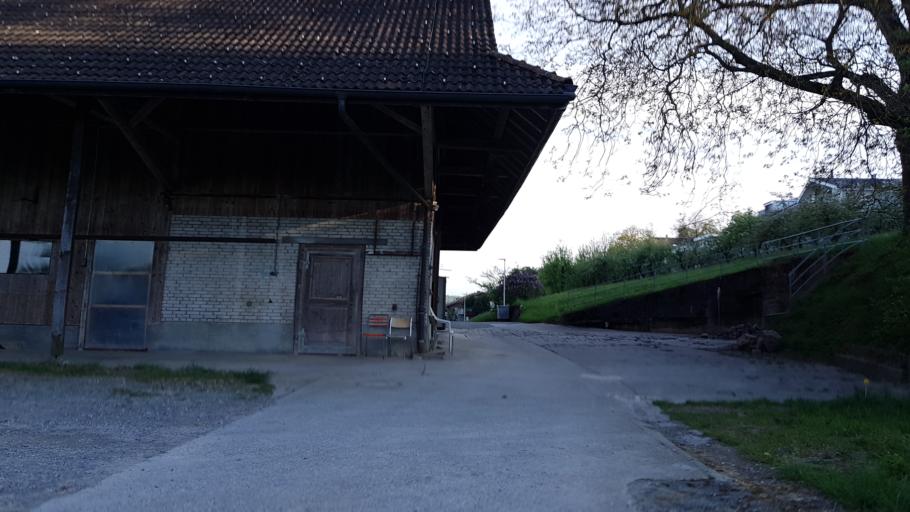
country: CH
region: Aargau
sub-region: Bezirk Kulm
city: Reinach
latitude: 47.2777
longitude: 8.1980
